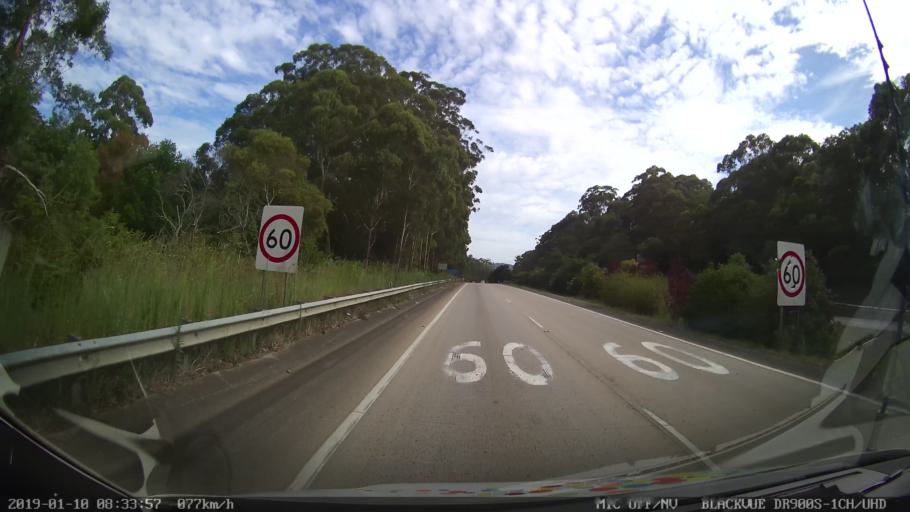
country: AU
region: New South Wales
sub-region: Coffs Harbour
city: Boambee
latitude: -30.3259
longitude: 153.0831
